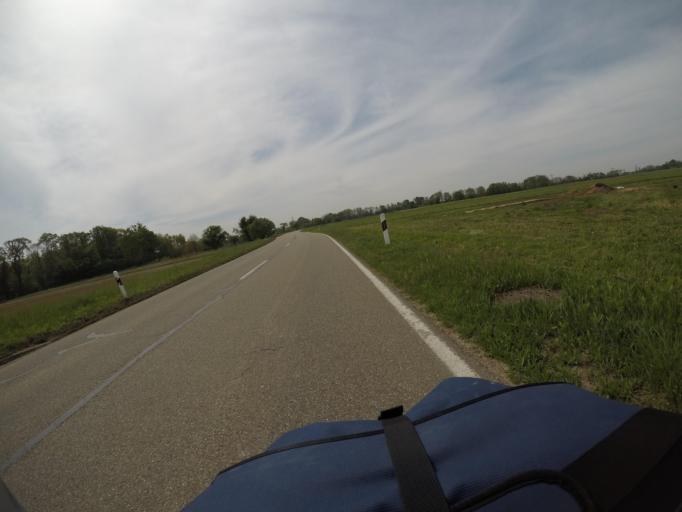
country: DE
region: Baden-Wuerttemberg
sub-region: Karlsruhe Region
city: Schwarzach
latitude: 48.7574
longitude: 8.0397
